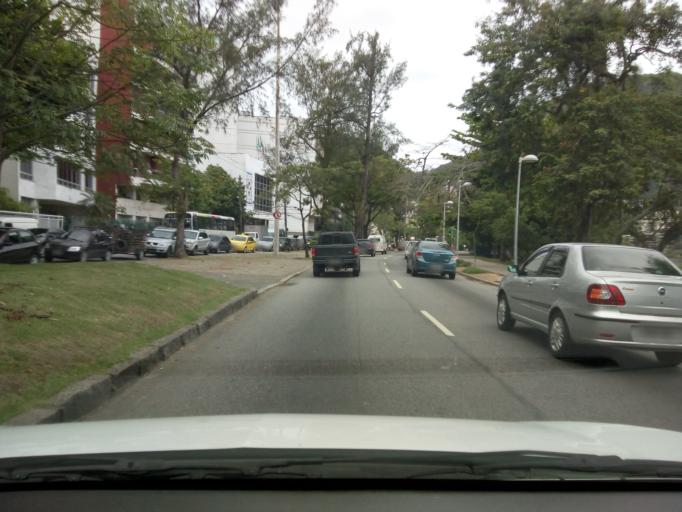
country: BR
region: Rio de Janeiro
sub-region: Rio De Janeiro
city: Rio de Janeiro
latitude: -22.9628
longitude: -43.2107
